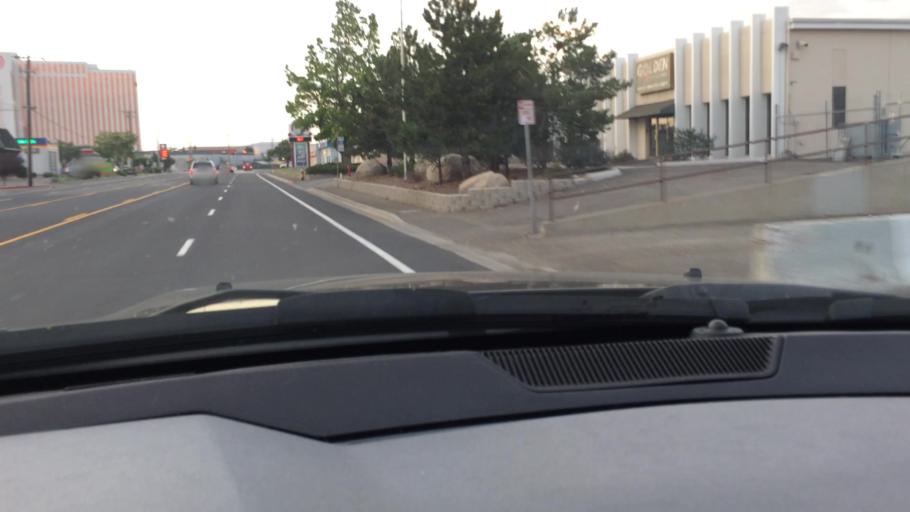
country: US
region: Nevada
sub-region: Washoe County
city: Sparks
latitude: 39.5151
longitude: -119.7774
